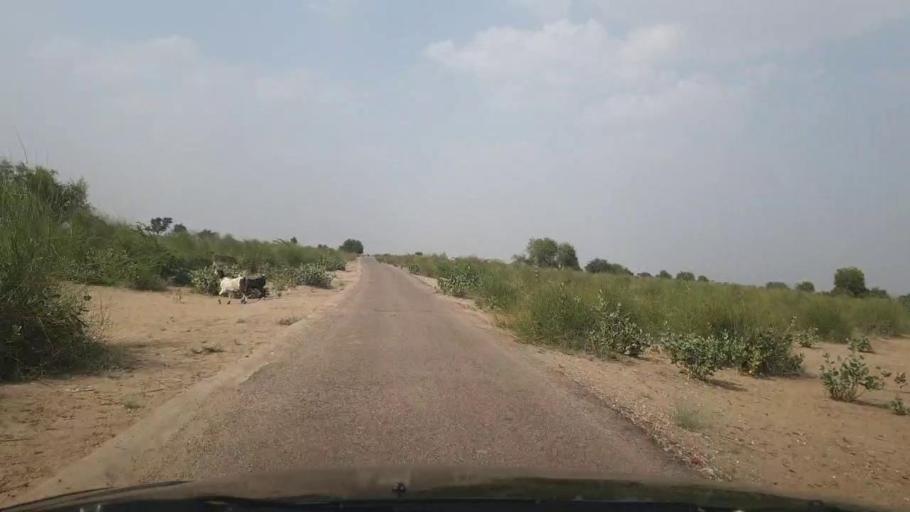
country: PK
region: Sindh
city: Islamkot
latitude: 24.9377
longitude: 70.5728
